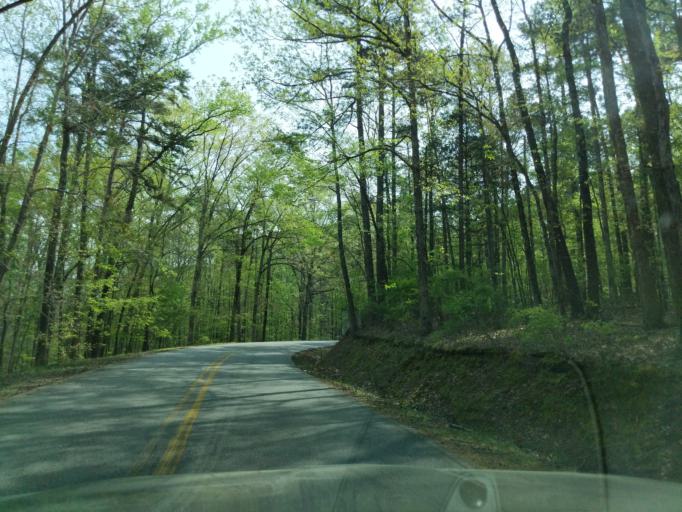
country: US
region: Georgia
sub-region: Lincoln County
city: Lincolnton
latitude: 33.8504
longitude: -82.4008
